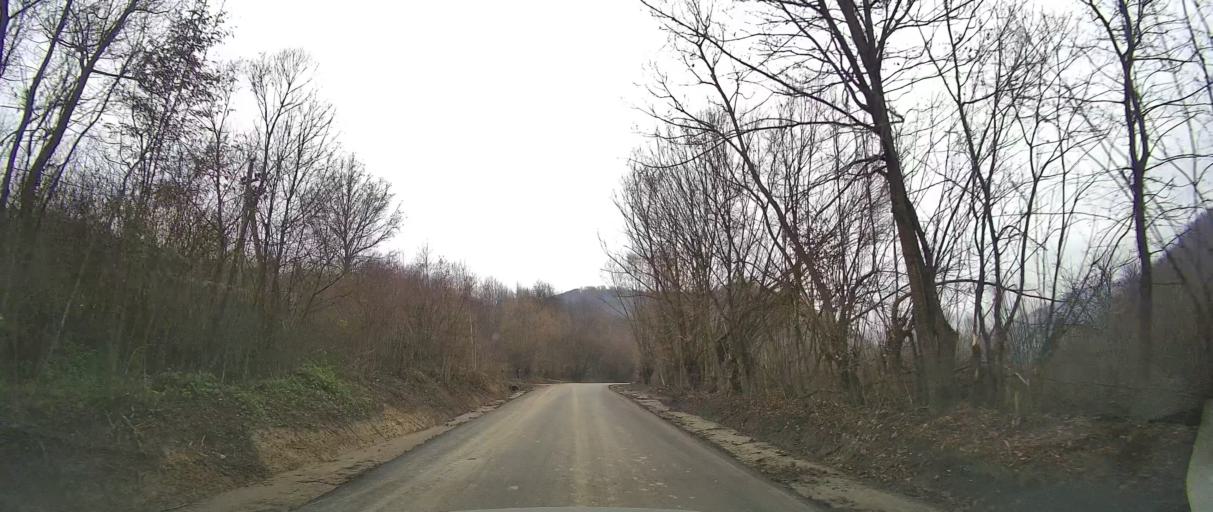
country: UA
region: Zakarpattia
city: Velykyi Bereznyi
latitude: 48.9544
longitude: 22.5465
